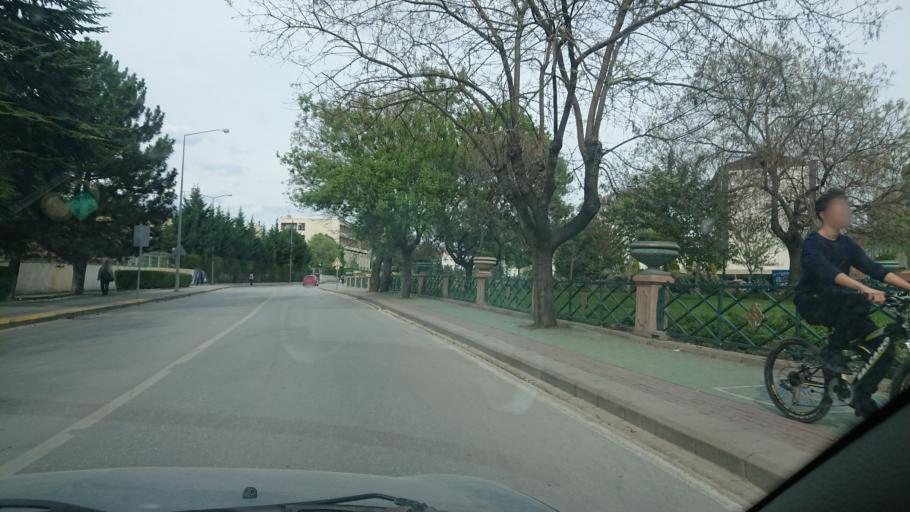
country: TR
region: Eskisehir
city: Eskisehir
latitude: 39.7746
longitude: 30.5034
